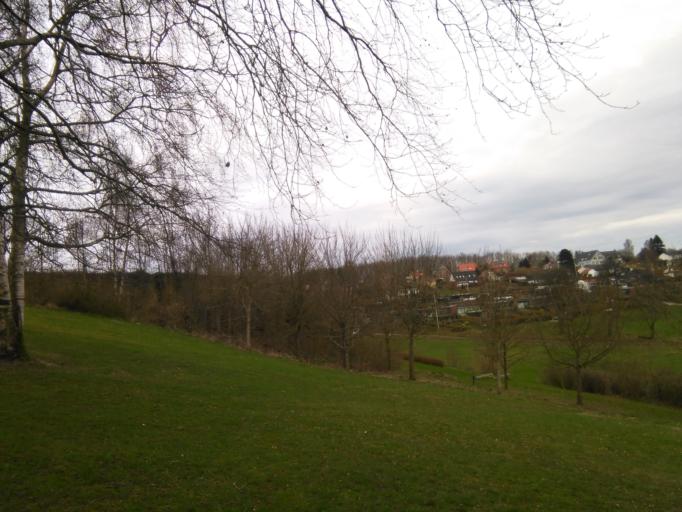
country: DK
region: Central Jutland
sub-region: Skanderborg Kommune
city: Stilling
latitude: 56.0605
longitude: 9.9904
